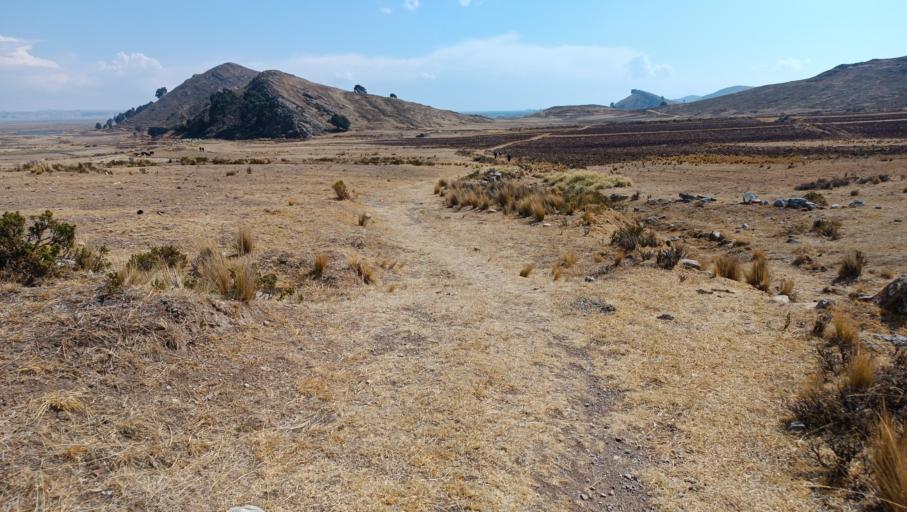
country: BO
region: La Paz
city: Batallas
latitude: -16.3477
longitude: -68.6615
